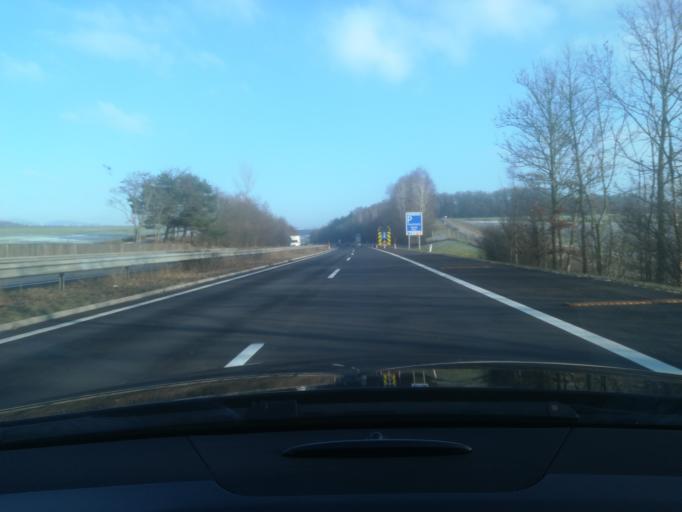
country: AT
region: Upper Austria
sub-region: Politischer Bezirk Urfahr-Umgebung
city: Engerwitzdorf
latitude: 48.3369
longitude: 14.4330
